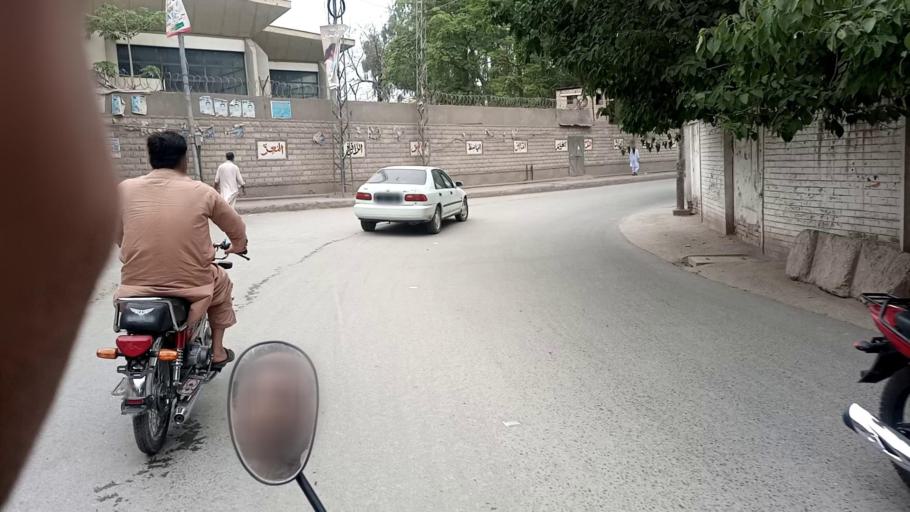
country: PK
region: Khyber Pakhtunkhwa
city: Peshawar
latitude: 33.9935
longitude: 71.5370
